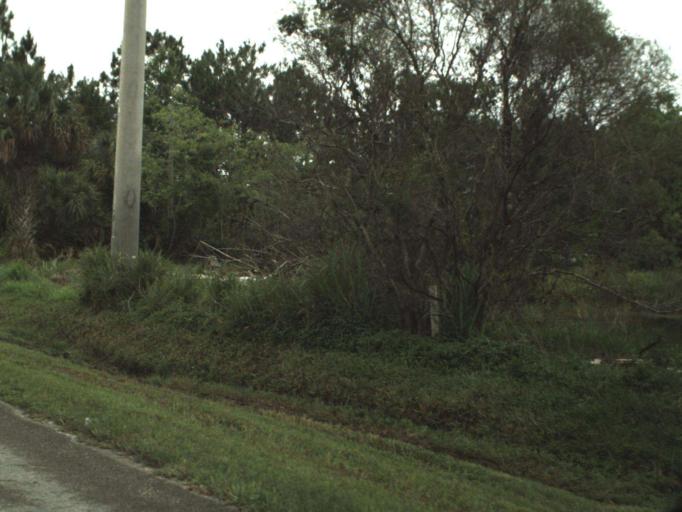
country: US
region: Florida
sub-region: Brevard County
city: Mims
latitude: 28.6660
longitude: -80.8884
